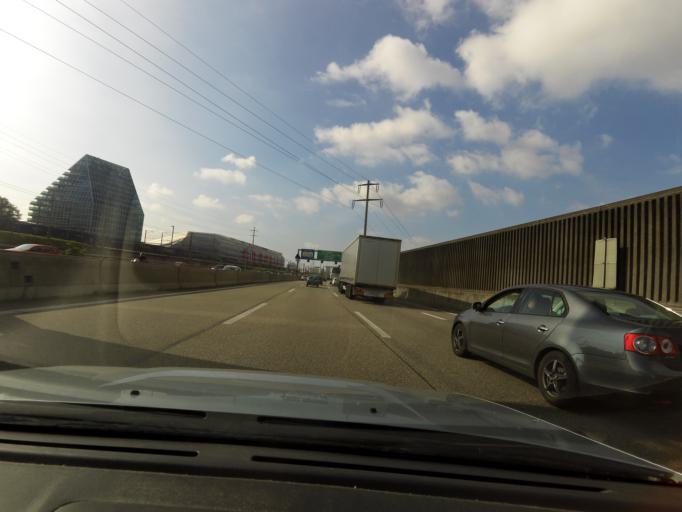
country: CH
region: Basel-Landschaft
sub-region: Bezirk Arlesheim
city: Birsfelden
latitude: 47.5421
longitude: 7.6247
